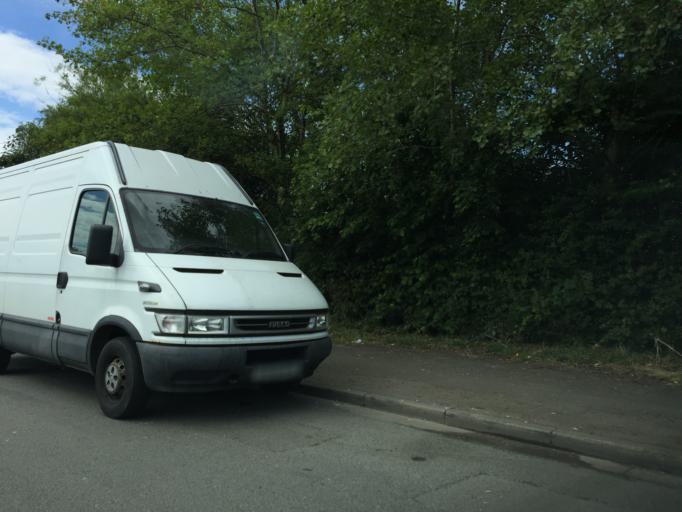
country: GB
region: Wales
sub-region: Newport
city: Nash
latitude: 51.5702
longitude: -2.9696
